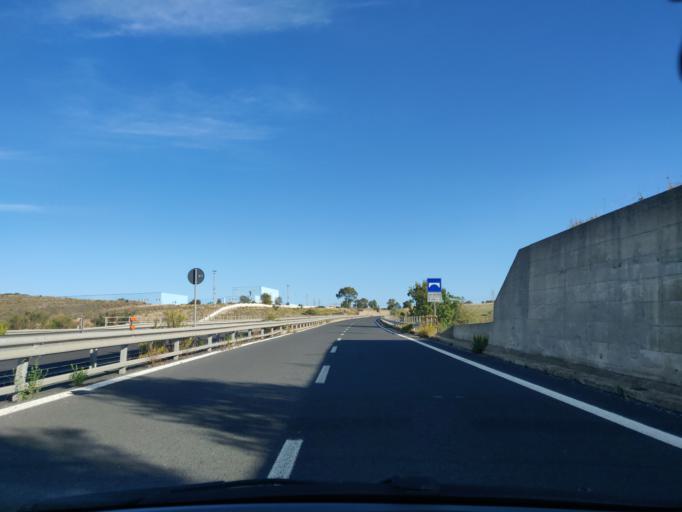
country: IT
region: Latium
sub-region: Citta metropolitana di Roma Capitale
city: Aurelia
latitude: 42.1207
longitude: 11.7911
